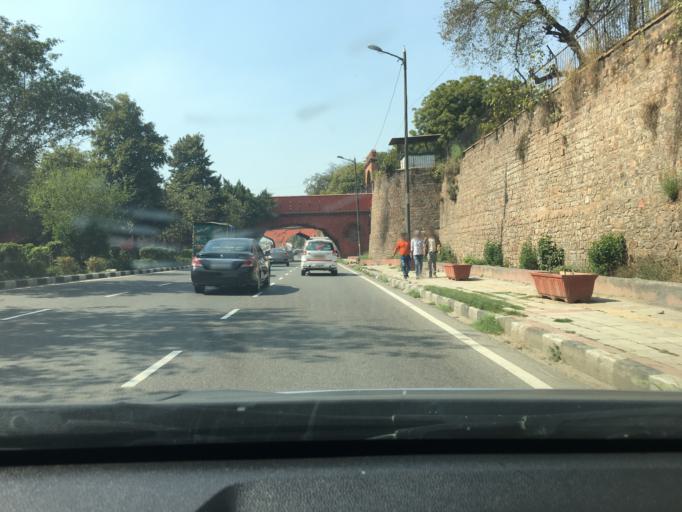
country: IN
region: NCT
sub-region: North Delhi
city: Delhi
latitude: 28.6599
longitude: 77.2430
